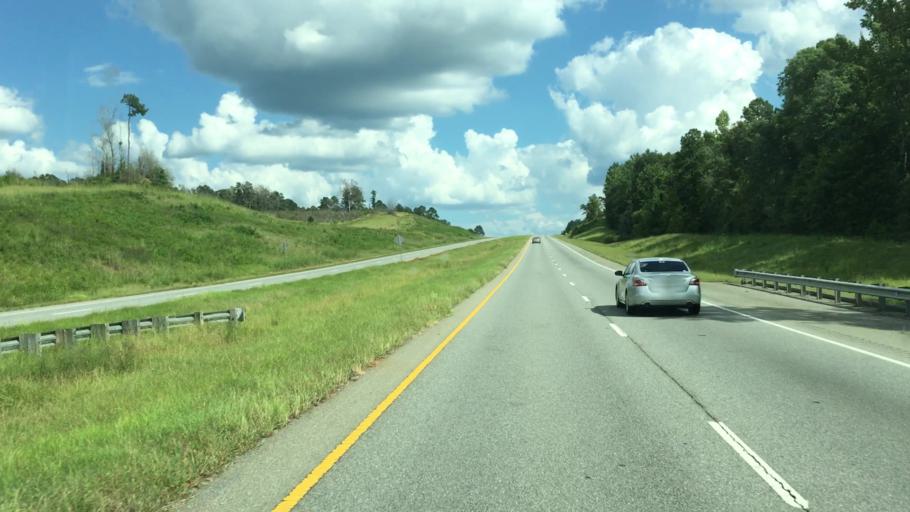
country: US
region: Georgia
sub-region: Wilkinson County
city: Irwinton
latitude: 32.7119
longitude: -83.1376
